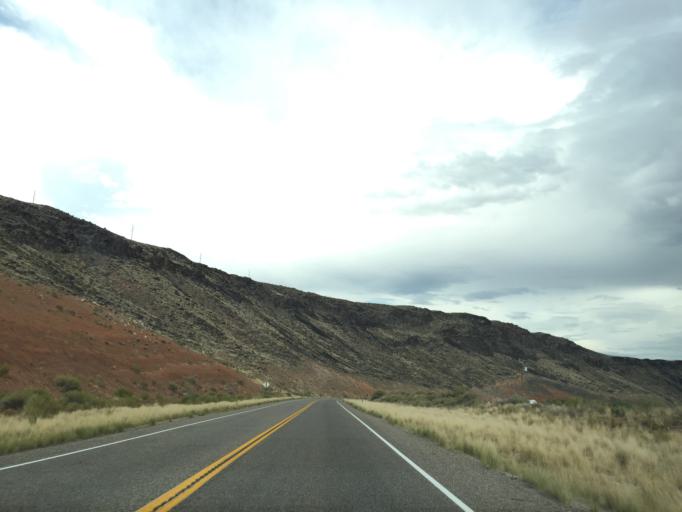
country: US
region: Utah
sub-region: Washington County
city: LaVerkin
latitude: 37.1952
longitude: -113.1520
